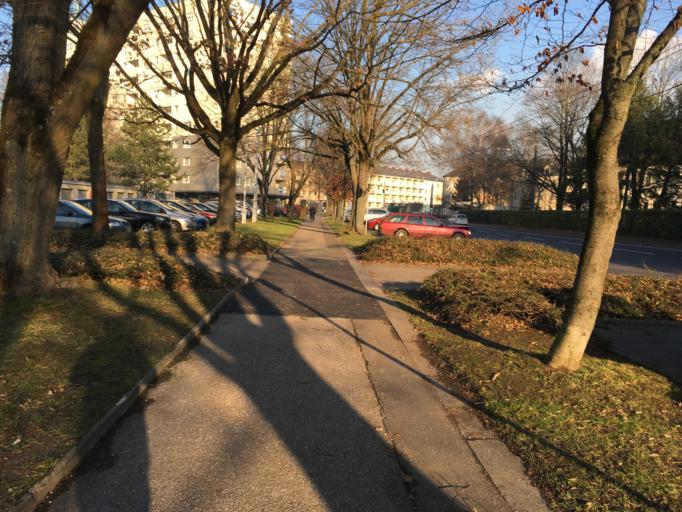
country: AT
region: Upper Austria
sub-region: Politischer Bezirk Linz-Land
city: Leonding
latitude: 48.2688
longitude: 14.2869
